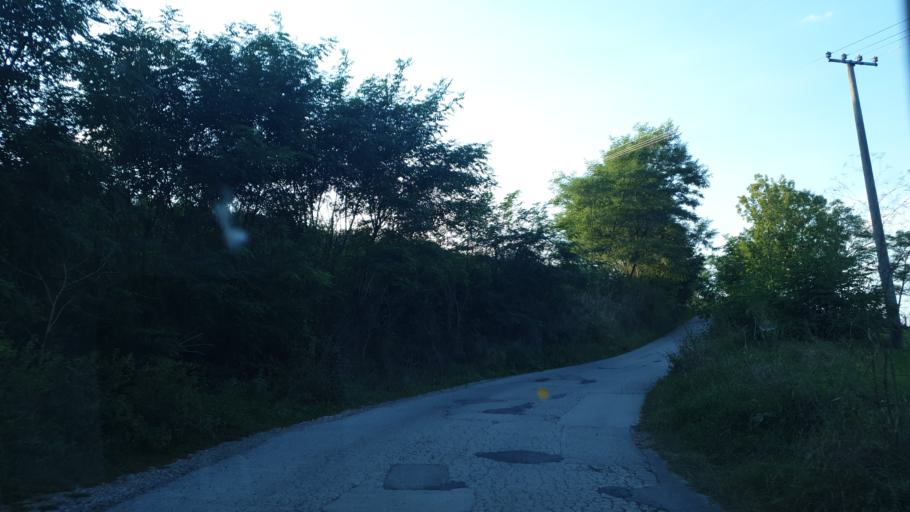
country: RS
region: Central Serbia
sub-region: Zlatiborski Okrug
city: Kosjeric
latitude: 43.9739
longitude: 20.0226
